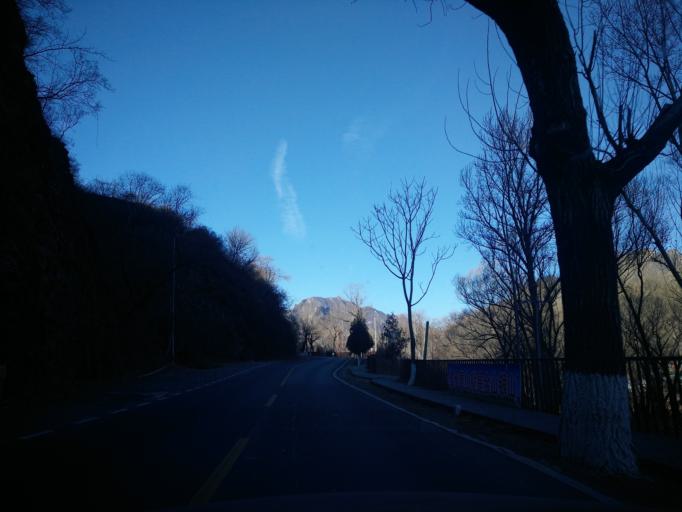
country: CN
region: Beijing
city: Yanchi
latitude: 40.0118
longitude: 115.8221
